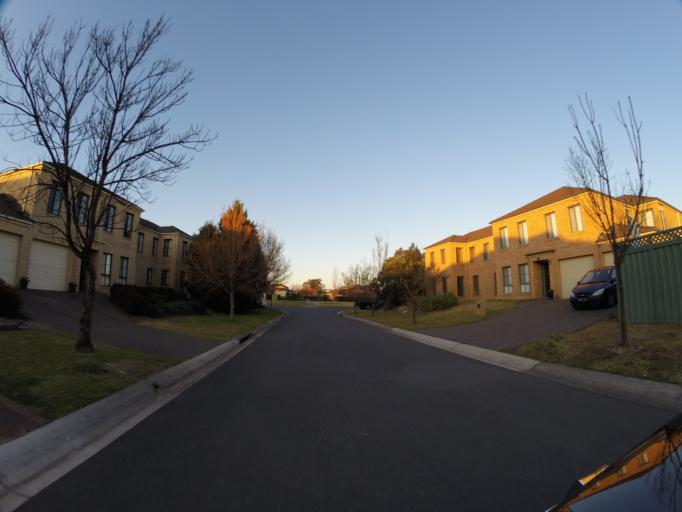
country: AU
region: New South Wales
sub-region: Camden
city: Narellan
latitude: -34.0254
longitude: 150.7285
